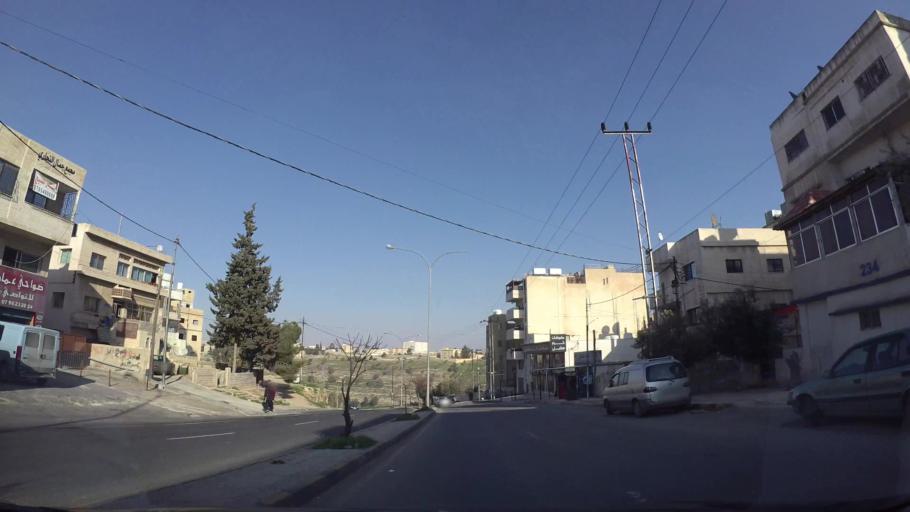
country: JO
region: Amman
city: Amman
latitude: 31.9740
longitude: 35.9674
